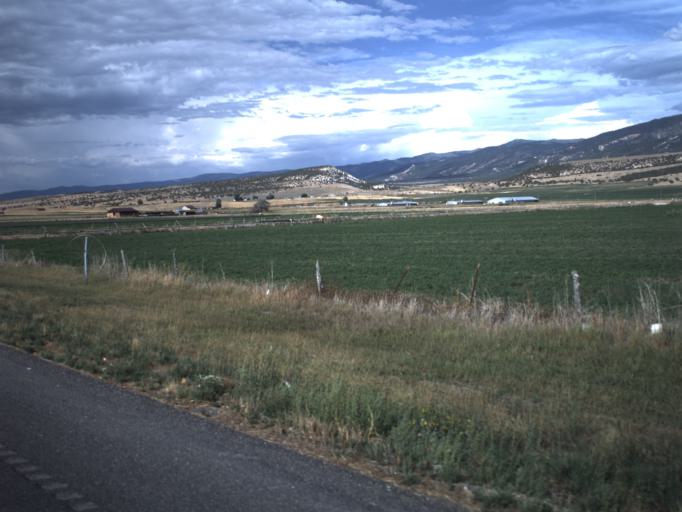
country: US
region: Utah
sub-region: Sanpete County
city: Ephraim
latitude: 39.3793
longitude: -111.5861
